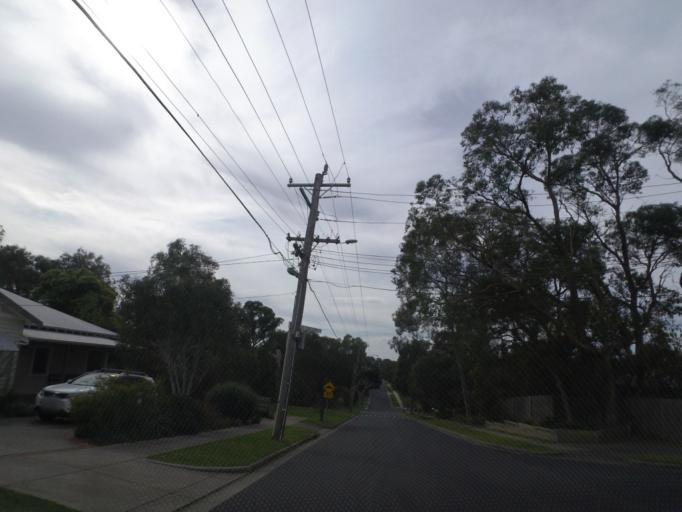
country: AU
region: Victoria
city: Mitcham
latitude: -37.8254
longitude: 145.2019
